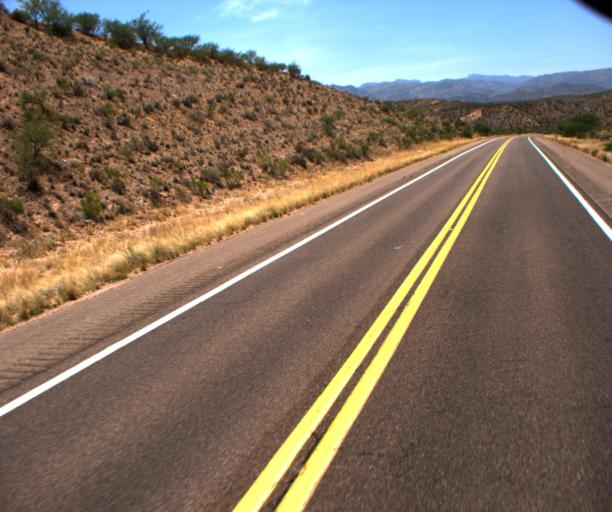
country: US
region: Arizona
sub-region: Gila County
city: Tonto Basin
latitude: 33.9184
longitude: -111.3162
